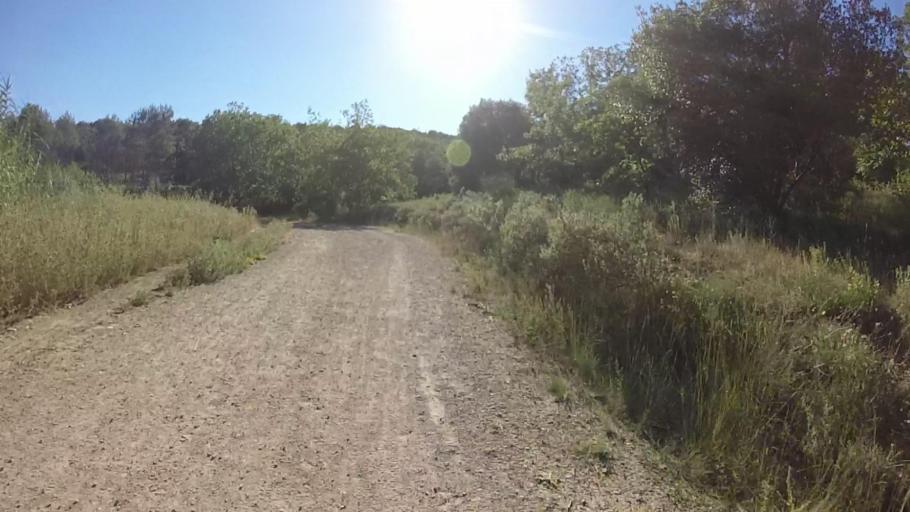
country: FR
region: Provence-Alpes-Cote d'Azur
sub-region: Departement des Alpes-Maritimes
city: Mougins
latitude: 43.6106
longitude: 7.0305
